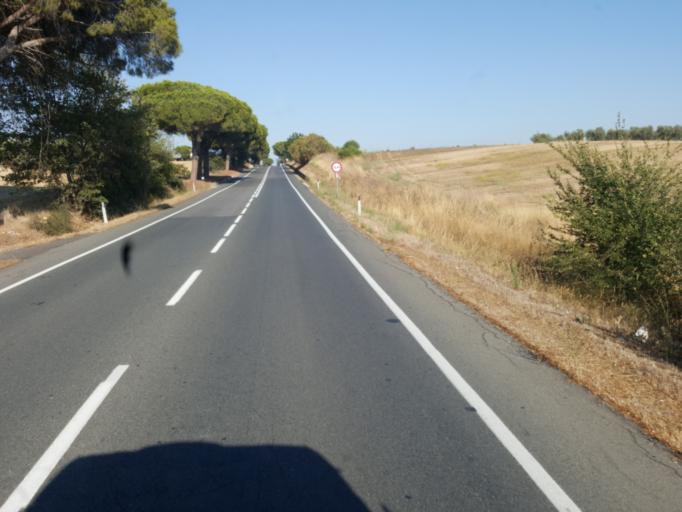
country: IT
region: Tuscany
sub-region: Provincia di Grosseto
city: Capalbio
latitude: 42.4145
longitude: 11.4356
